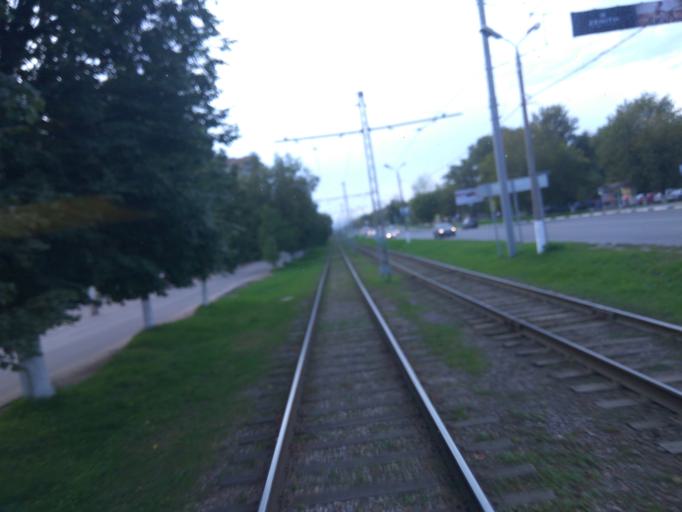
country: RU
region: Moskovskaya
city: Kolomna
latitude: 55.0865
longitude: 38.7944
